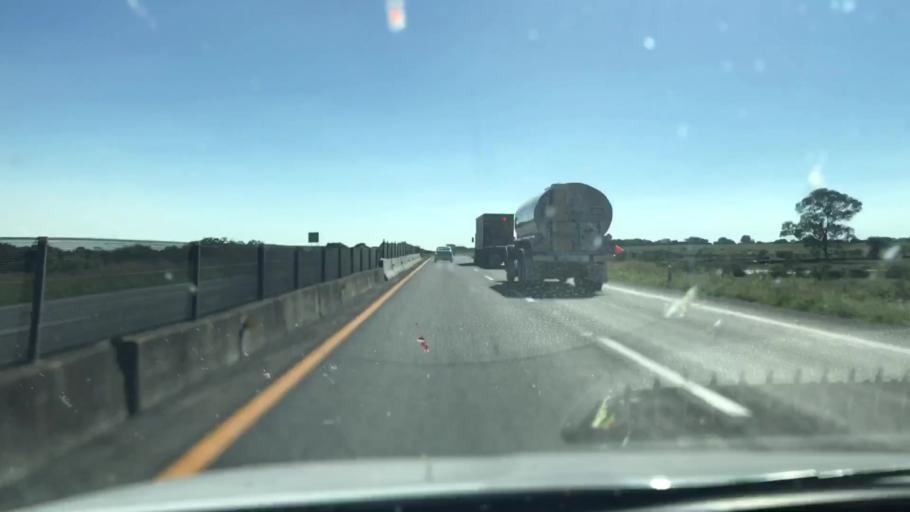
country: MX
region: Jalisco
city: Tepatitlan de Morelos
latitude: 20.8620
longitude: -102.7625
